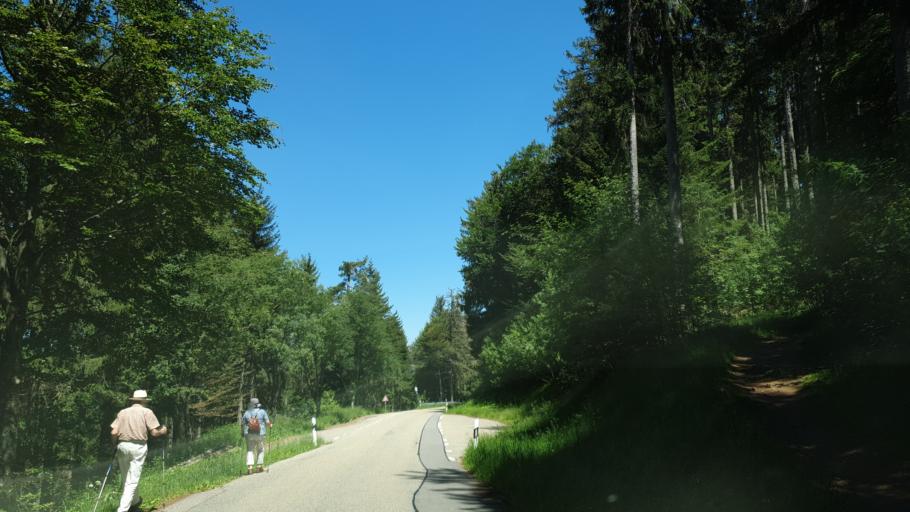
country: DE
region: Baden-Wuerttemberg
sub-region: Freiburg Region
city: Horben
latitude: 47.9012
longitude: 7.8667
